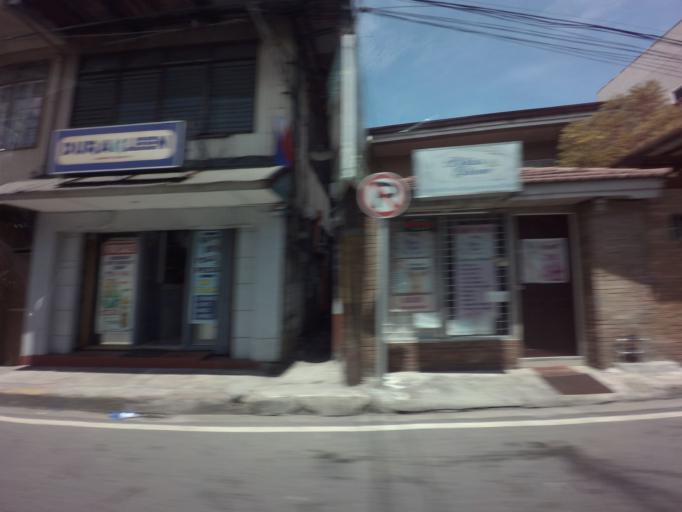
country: PH
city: Sambayanihan People's Village
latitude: 14.5030
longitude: 120.9932
